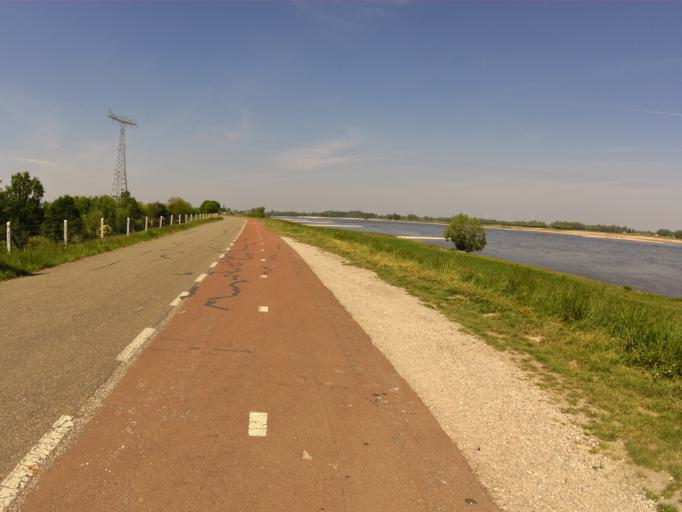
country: NL
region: Gelderland
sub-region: Gemeente Neerijnen
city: Neerijnen
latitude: 51.8071
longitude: 5.3322
